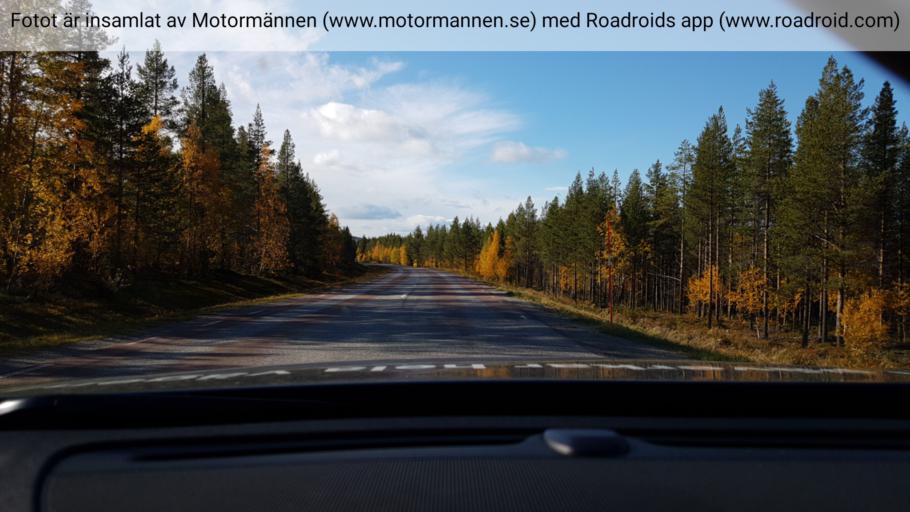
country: SE
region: Norrbotten
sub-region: Arjeplogs Kommun
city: Arjeplog
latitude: 66.0593
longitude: 17.9410
